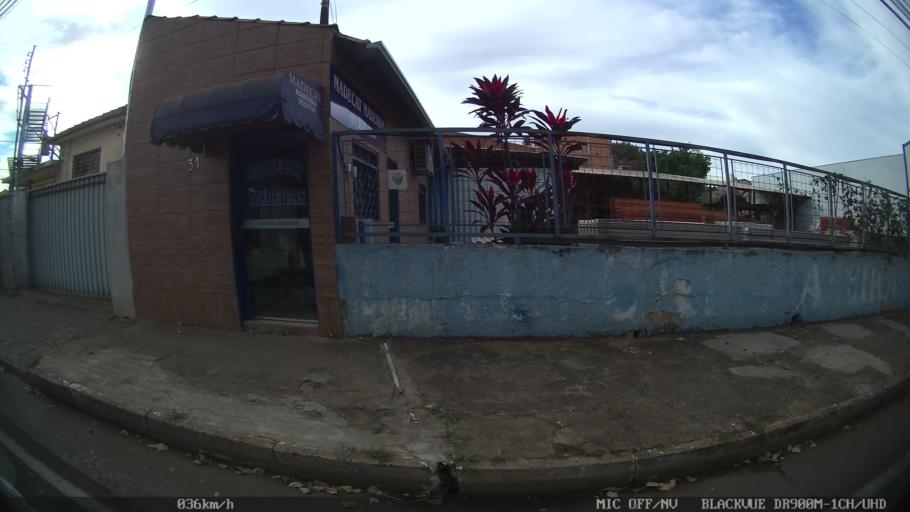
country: BR
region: Sao Paulo
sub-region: Catanduva
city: Catanduva
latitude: -21.1316
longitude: -48.9688
